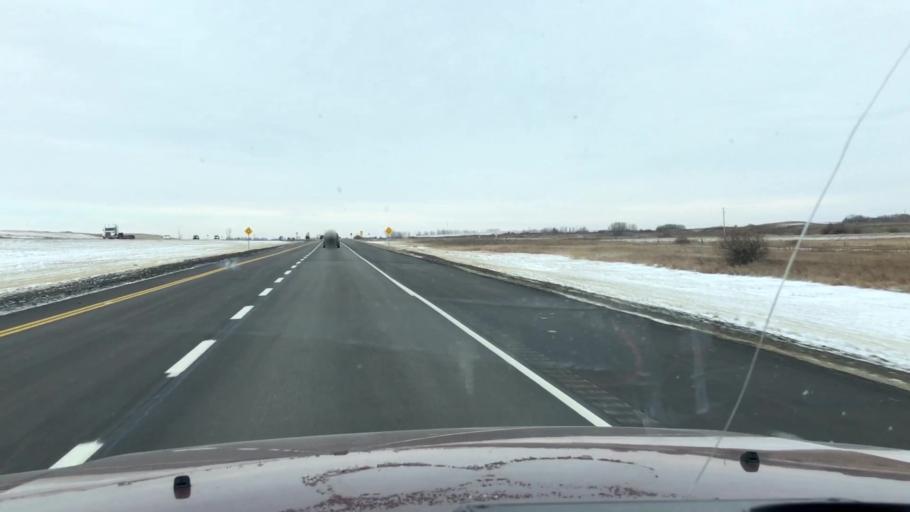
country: CA
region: Saskatchewan
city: Moose Jaw
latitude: 50.8648
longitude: -105.5957
